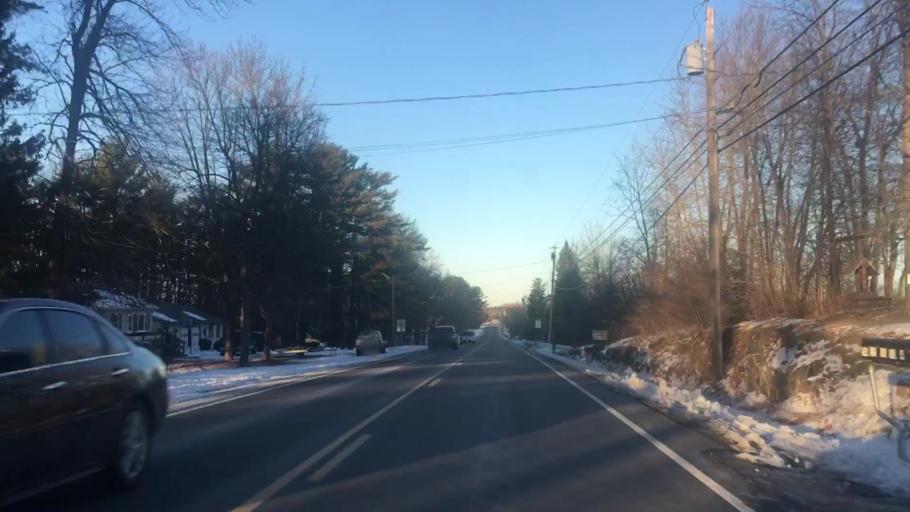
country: US
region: Maine
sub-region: Kennebec County
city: Benton
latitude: 44.5879
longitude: -69.5447
